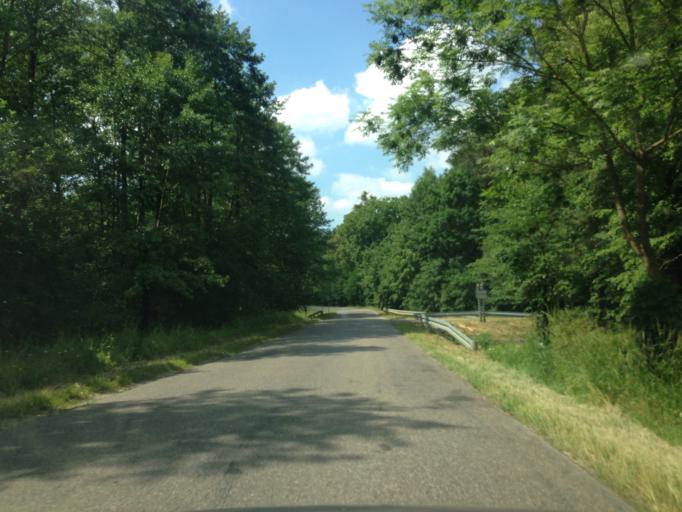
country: PL
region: Kujawsko-Pomorskie
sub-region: Powiat brodnicki
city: Bartniczka
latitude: 53.2377
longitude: 19.6230
